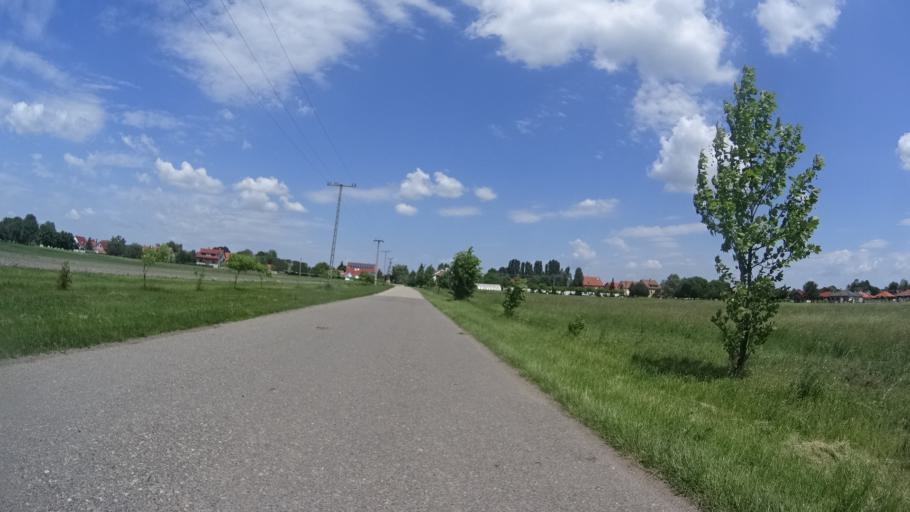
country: HU
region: Bacs-Kiskun
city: Tiszakecske
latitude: 46.9420
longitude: 20.0920
